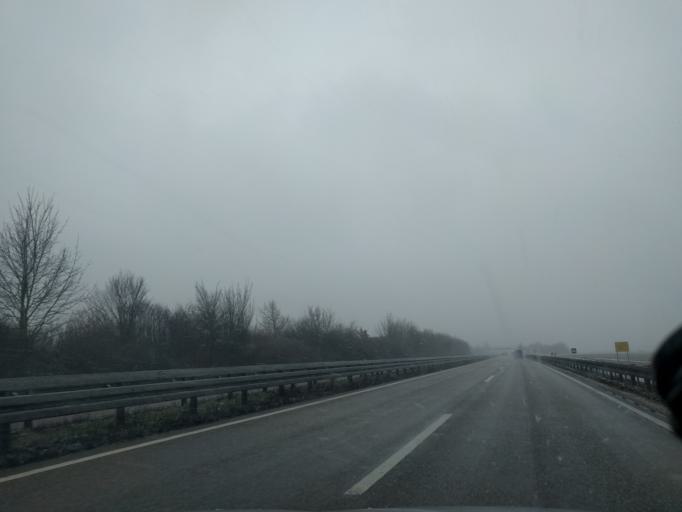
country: DE
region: Bavaria
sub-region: Swabia
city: Nordendorf
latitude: 48.5982
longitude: 10.8400
